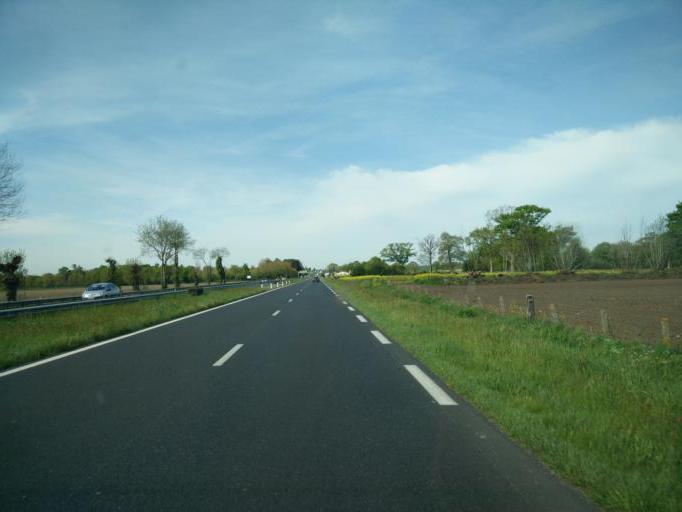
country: FR
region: Lower Normandy
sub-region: Departement de la Manche
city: Le Val-Saint-Pere
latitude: 48.5902
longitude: -1.4206
